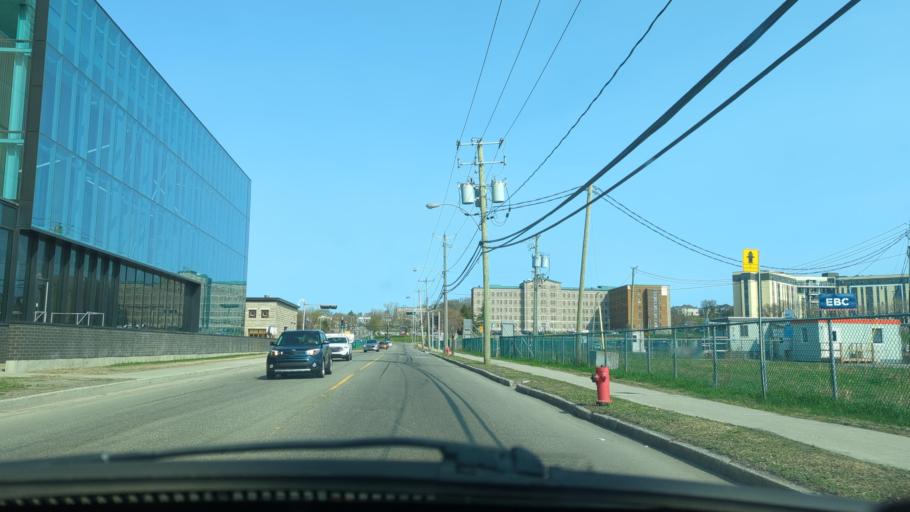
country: CA
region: Quebec
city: Quebec
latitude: 46.8492
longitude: -71.2204
